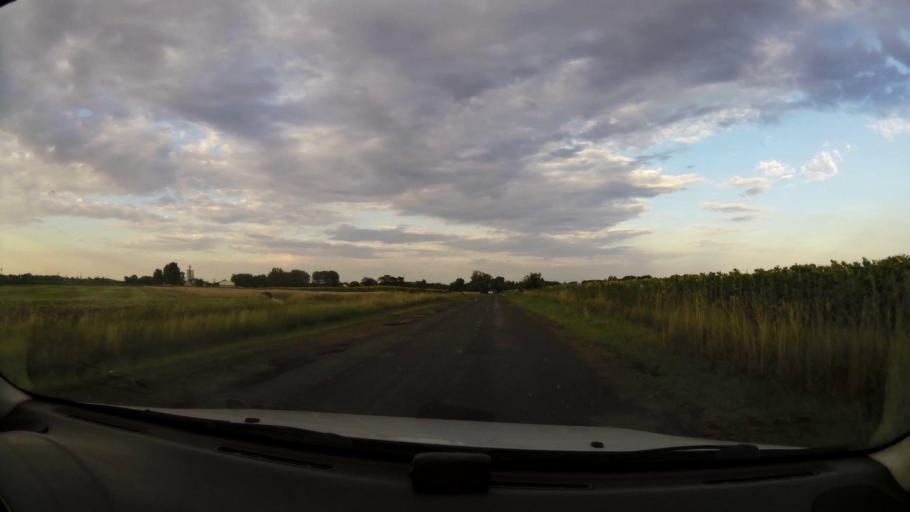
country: HU
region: Pest
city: Tapioszolos
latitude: 47.3210
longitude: 19.8612
